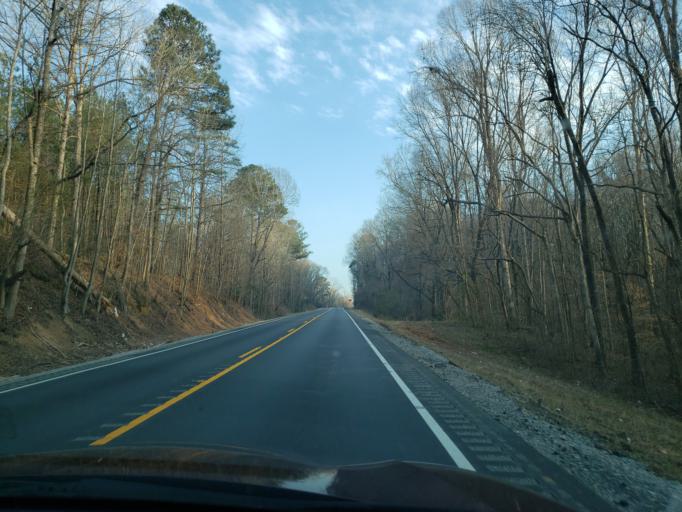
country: US
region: Alabama
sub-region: Hale County
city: Greensboro
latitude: 32.8131
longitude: -87.5964
